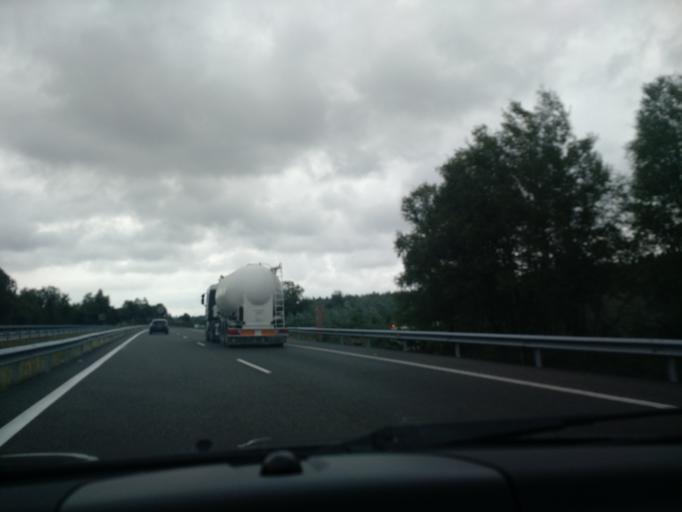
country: ES
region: Galicia
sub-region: Provincia da Coruna
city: Ordes
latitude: 43.0407
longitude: -8.3862
